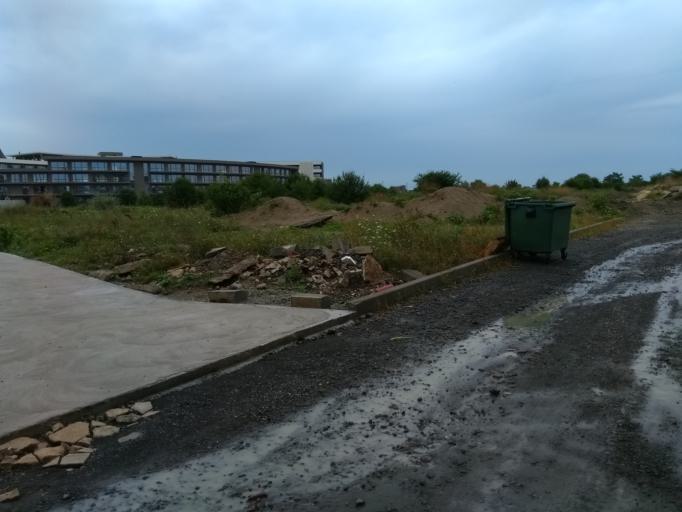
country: BG
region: Burgas
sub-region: Obshtina Nesebur
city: Ravda
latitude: 42.6552
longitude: 27.6896
